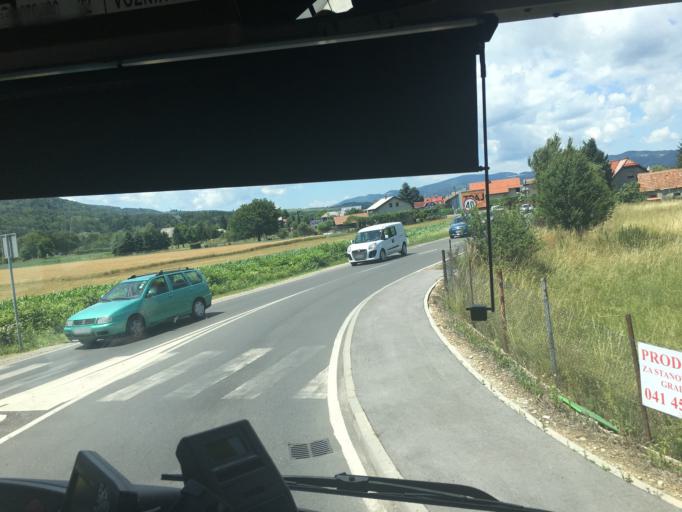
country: SI
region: Maribor
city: Razvanje
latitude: 46.5325
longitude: 15.6336
